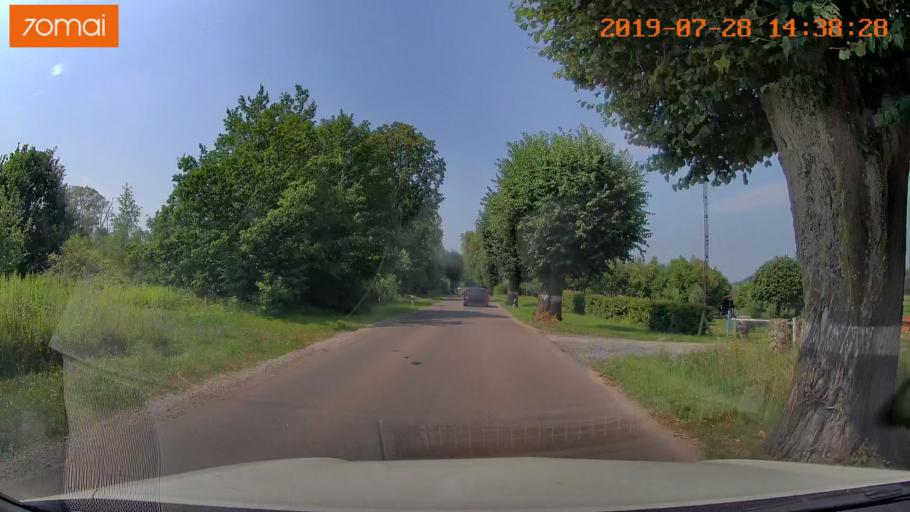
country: RU
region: Kaliningrad
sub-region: Gorod Kaliningrad
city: Yantarnyy
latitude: 54.8449
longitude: 19.9836
